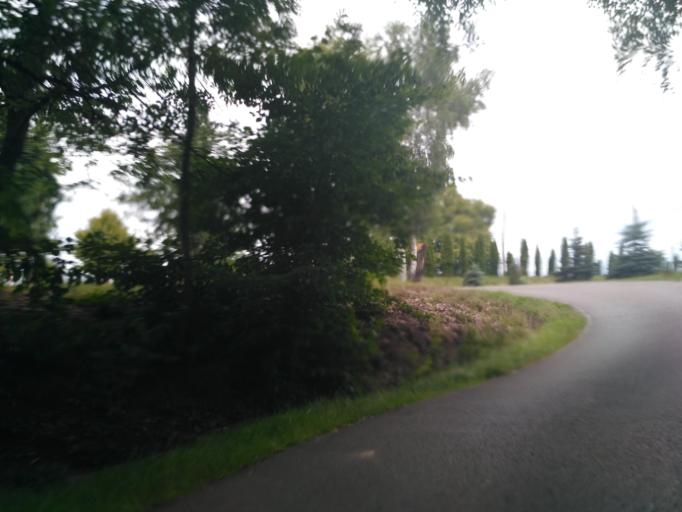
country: PL
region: Subcarpathian Voivodeship
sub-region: Powiat rzeszowski
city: Straszydle
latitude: 49.8933
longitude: 21.9421
